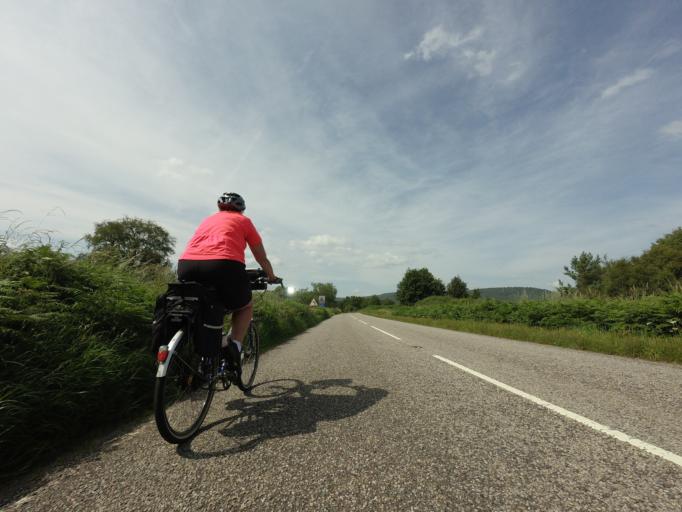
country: GB
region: Scotland
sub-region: Highland
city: Alness
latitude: 57.8572
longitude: -4.2304
